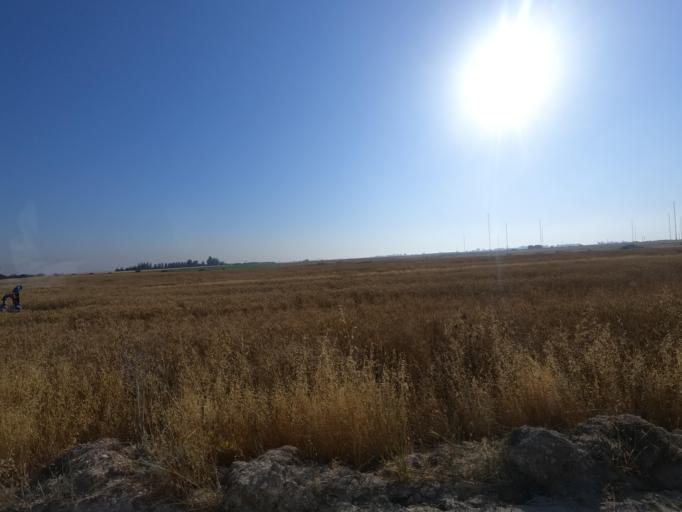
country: CY
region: Ammochostos
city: Acheritou
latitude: 35.0971
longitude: 33.8862
